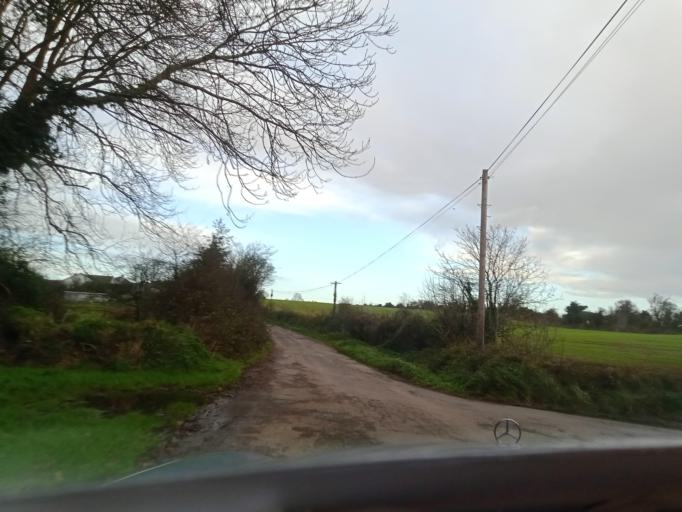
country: IE
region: Munster
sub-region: Waterford
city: Waterford
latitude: 52.3325
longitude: -7.0366
